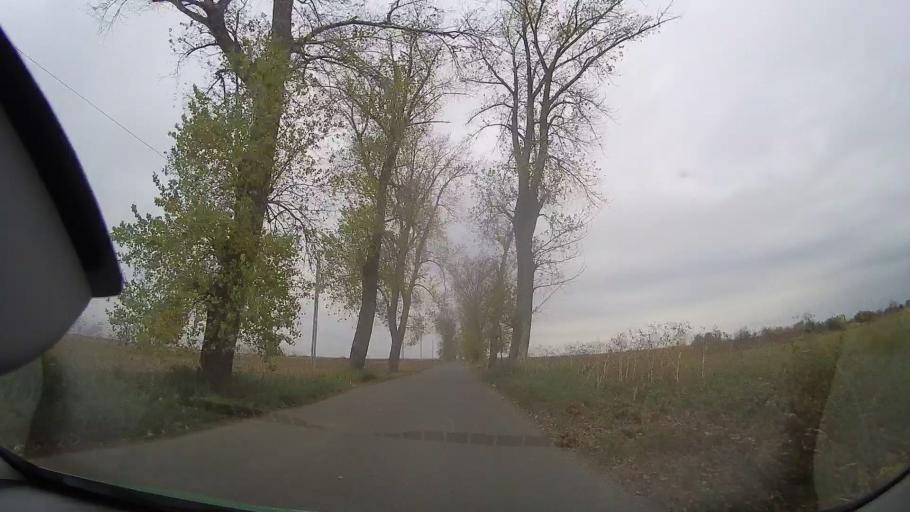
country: RO
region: Braila
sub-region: Comuna Ciocile
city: Ciocile
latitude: 44.8135
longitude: 27.2864
